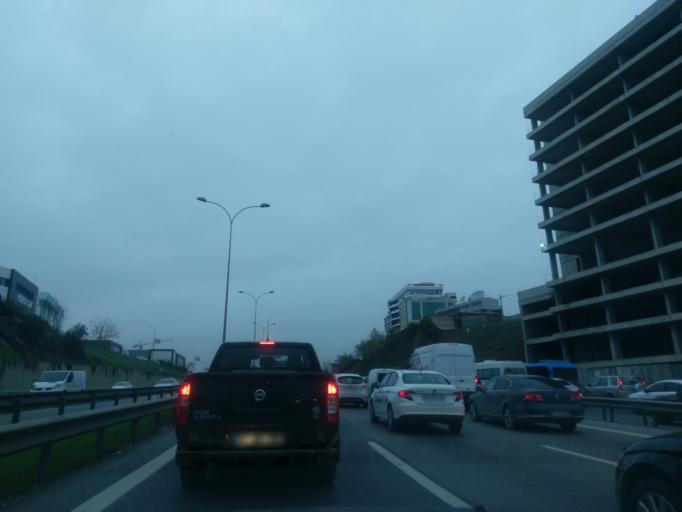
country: TR
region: Istanbul
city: Maltepe
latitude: 40.9457
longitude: 29.1268
